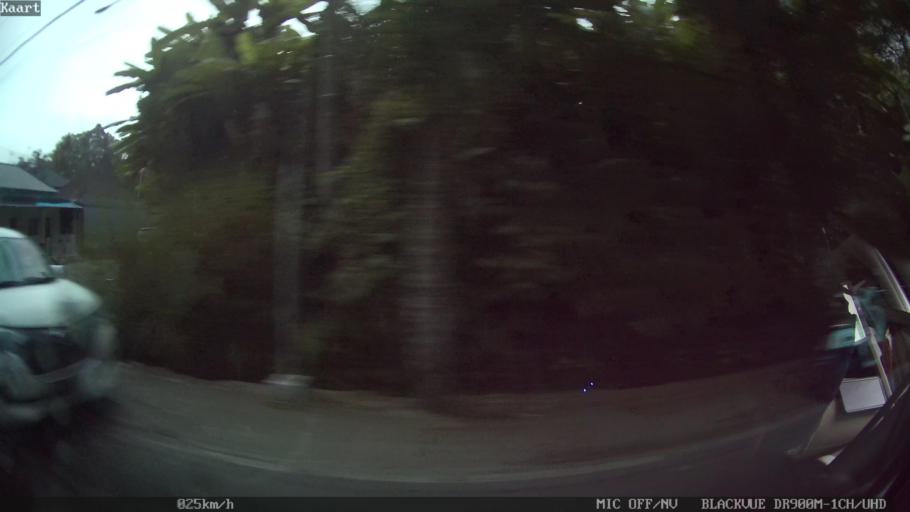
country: ID
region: Bali
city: Banjar Buahan
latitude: -8.4031
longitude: 115.2473
